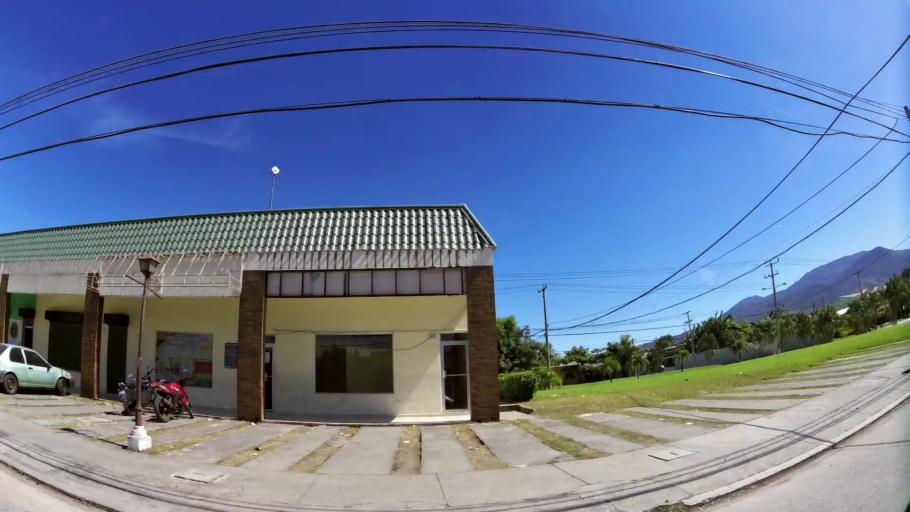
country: SV
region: La Libertad
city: San Juan Opico
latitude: 13.7935
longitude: -89.3599
